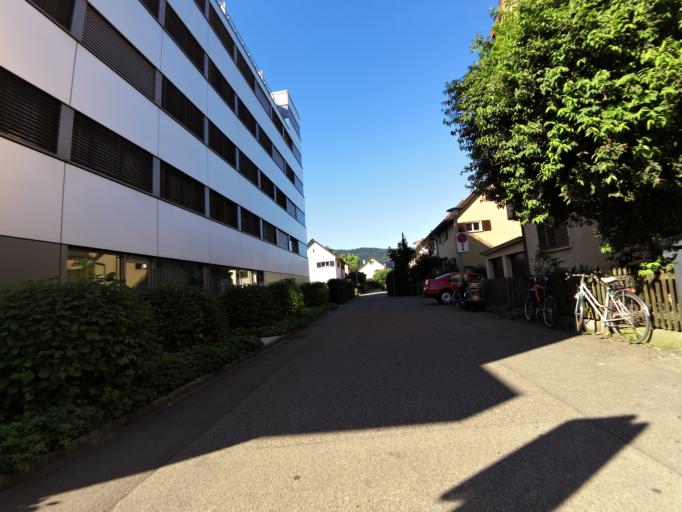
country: CH
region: Zurich
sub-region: Bezirk Zuerich
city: Zuerich (Kreis 4) / Hard
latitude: 47.3826
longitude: 8.5005
